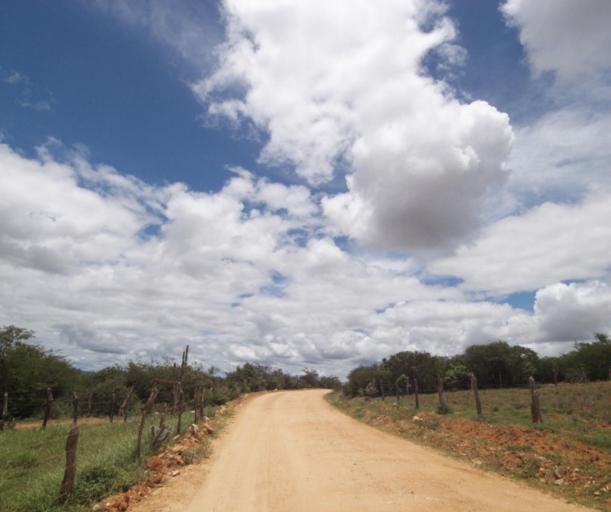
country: BR
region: Bahia
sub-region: Tanhacu
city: Tanhacu
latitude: -14.1583
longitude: -41.1832
